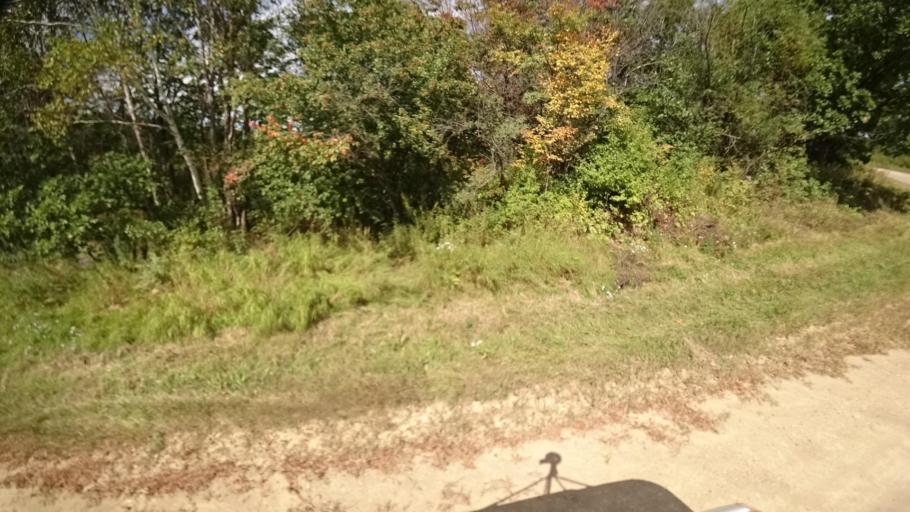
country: RU
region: Primorskiy
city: Yakovlevka
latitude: 44.7051
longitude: 133.6420
